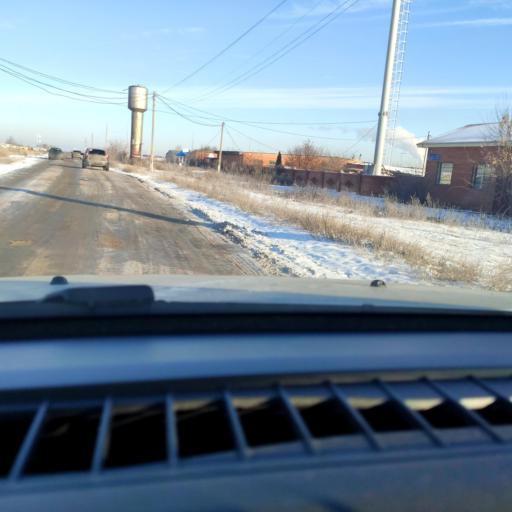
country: RU
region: Samara
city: Podstepki
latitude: 53.5206
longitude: 49.1454
